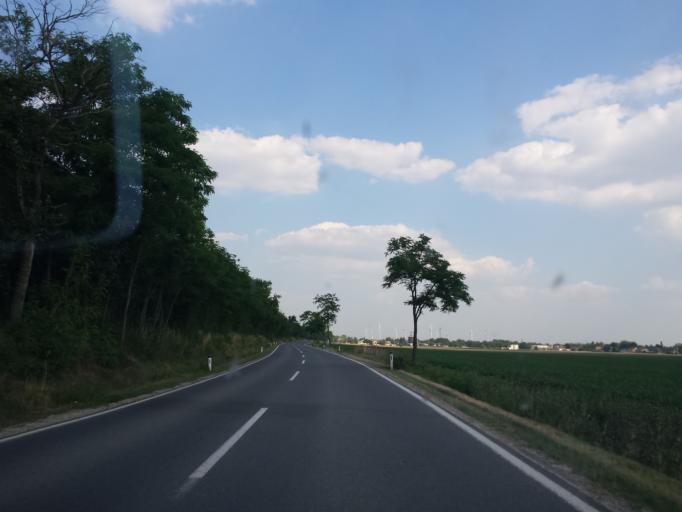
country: AT
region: Lower Austria
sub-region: Politischer Bezirk Ganserndorf
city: Grosshofen
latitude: 48.2749
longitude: 16.6154
